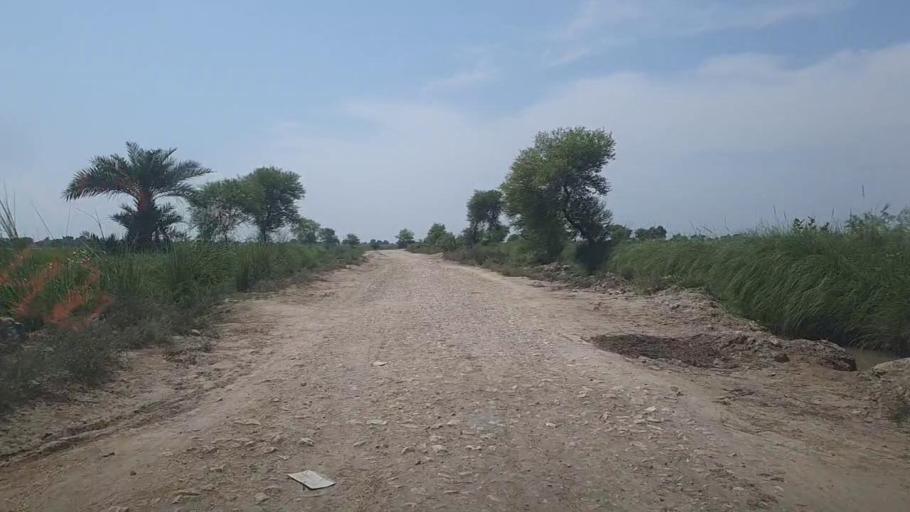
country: PK
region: Sindh
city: Kandhkot
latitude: 28.3100
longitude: 69.2370
